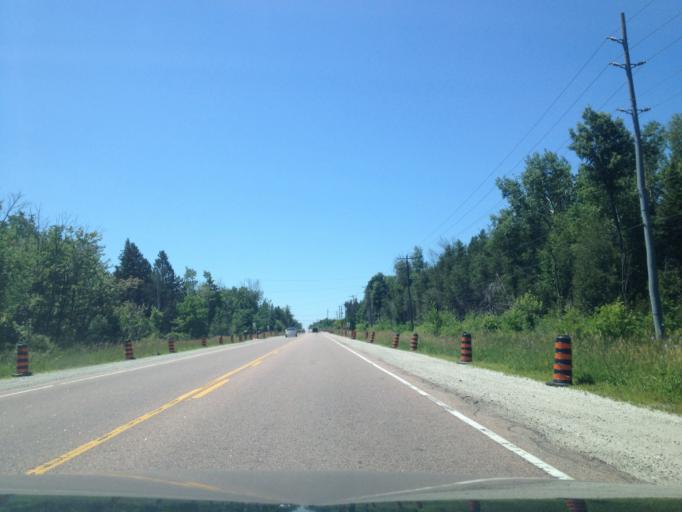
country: CA
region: Ontario
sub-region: Halton
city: Milton
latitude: 43.6719
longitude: -79.9899
